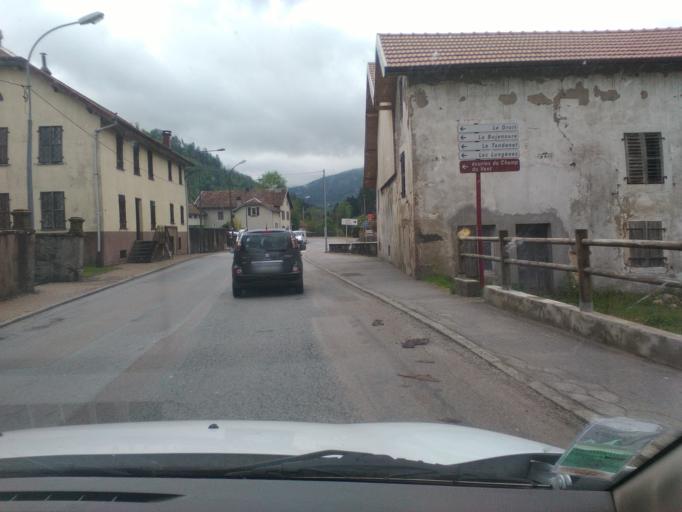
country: FR
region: Lorraine
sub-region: Departement des Vosges
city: Vagney
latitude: 47.9710
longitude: 6.7304
